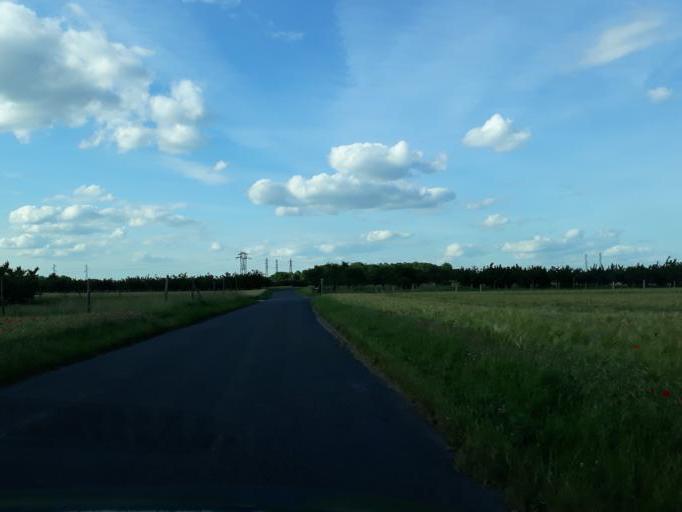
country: FR
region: Centre
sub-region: Departement du Loiret
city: Saint-Hilaire-Saint-Mesmin
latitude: 47.8477
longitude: 1.8233
